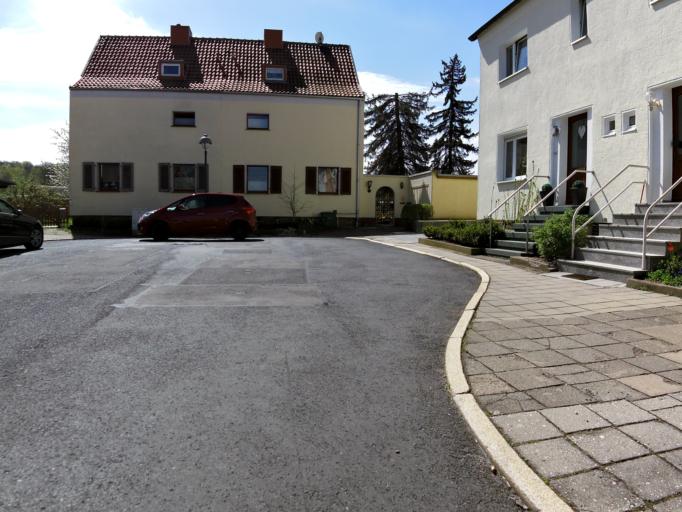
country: DE
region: Thuringia
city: Gotha
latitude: 50.9415
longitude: 10.7208
